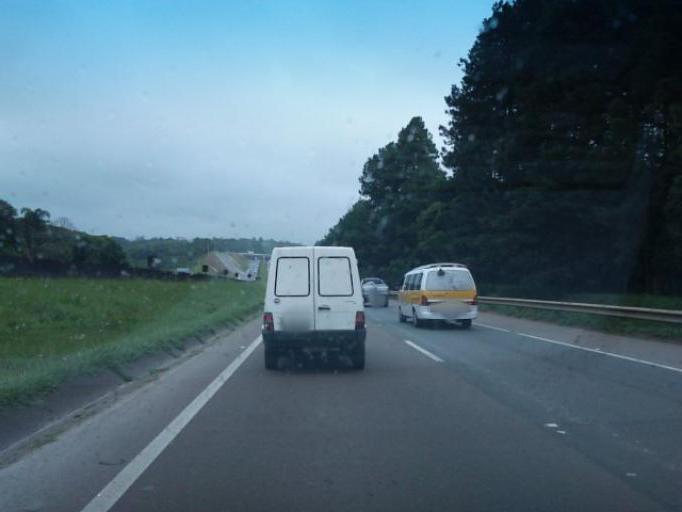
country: BR
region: Parana
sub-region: Sao Jose Dos Pinhais
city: Sao Jose dos Pinhais
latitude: -25.7753
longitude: -49.1206
